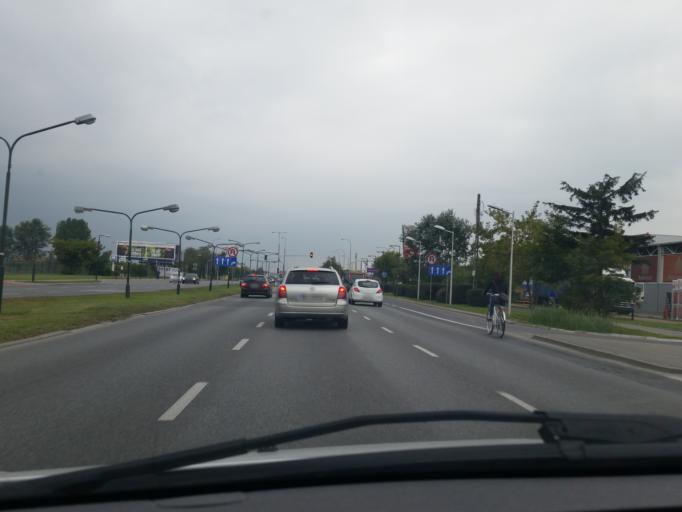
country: PL
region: Masovian Voivodeship
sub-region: Warszawa
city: Wlochy
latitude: 52.1728
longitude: 20.9401
